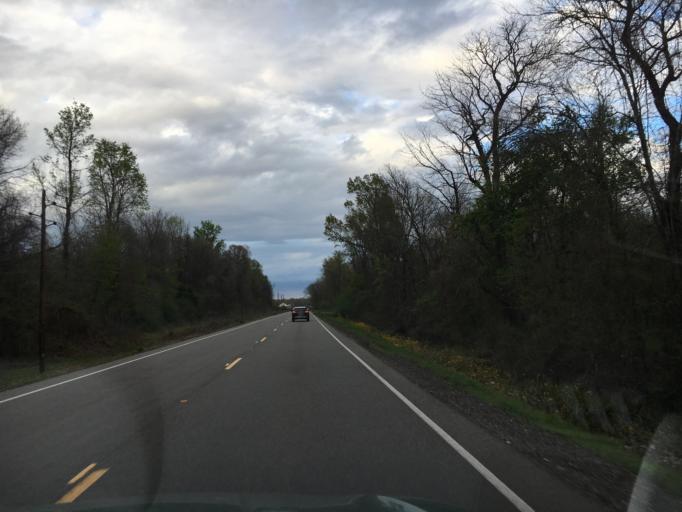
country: US
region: Louisiana
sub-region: West Baton Rouge Parish
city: Erwinville
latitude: 30.4735
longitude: -91.3960
